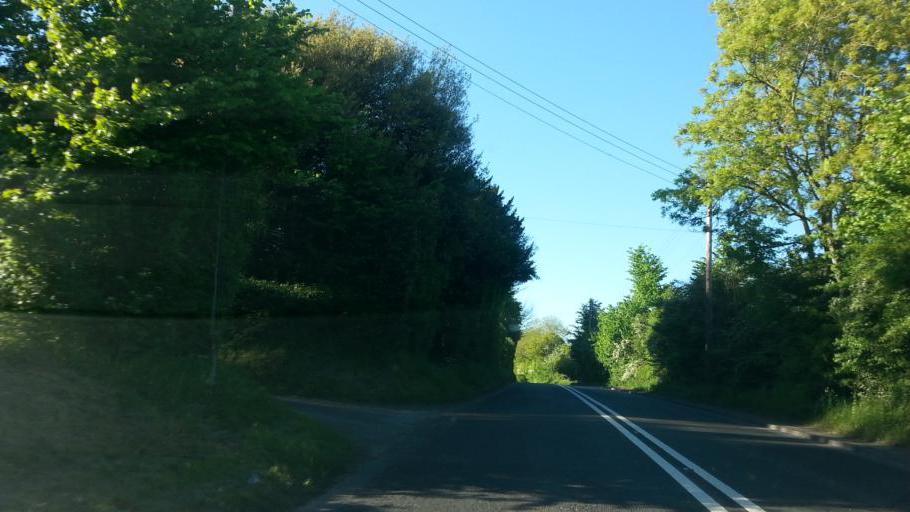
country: GB
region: England
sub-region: Bath and North East Somerset
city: Publow
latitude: 51.3812
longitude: -2.5518
